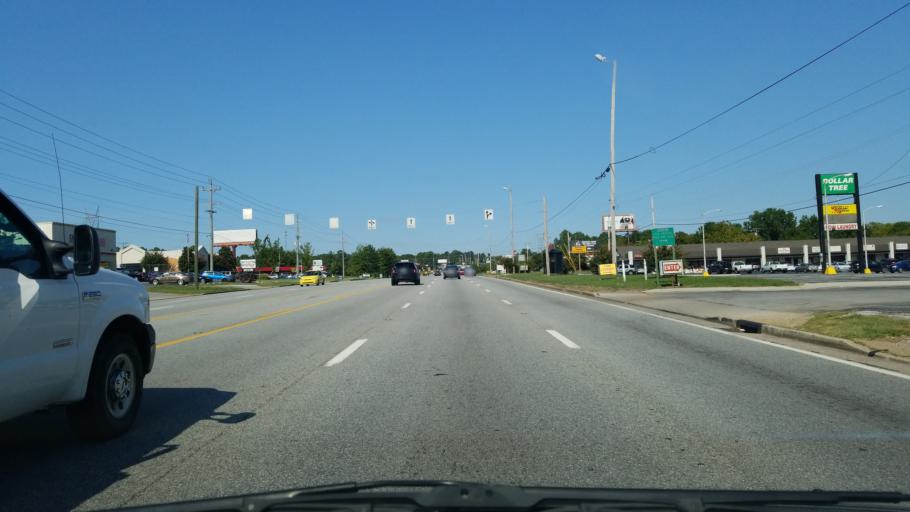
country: US
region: Tennessee
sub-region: Hamilton County
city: Harrison
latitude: 35.0873
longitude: -85.1900
